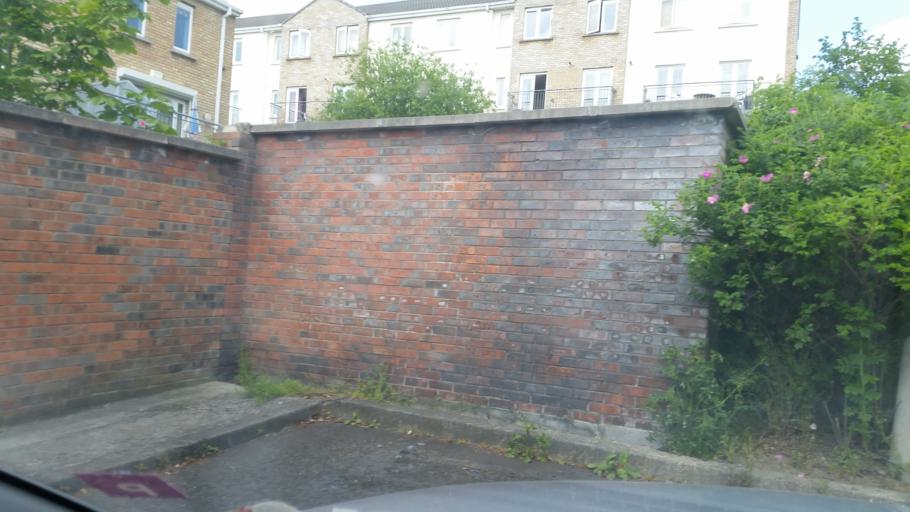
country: IE
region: Leinster
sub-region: Fingal County
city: Blanchardstown
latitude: 53.3940
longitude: -6.3743
